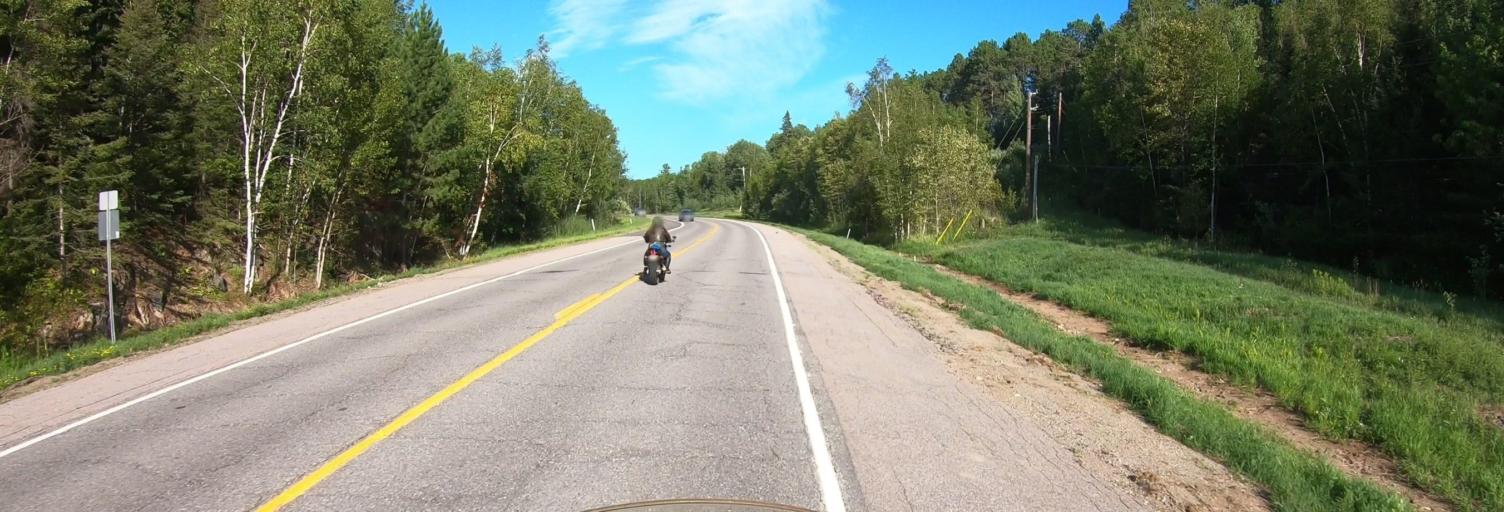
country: US
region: Minnesota
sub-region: Saint Louis County
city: Ely
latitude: 47.9247
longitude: -91.7829
